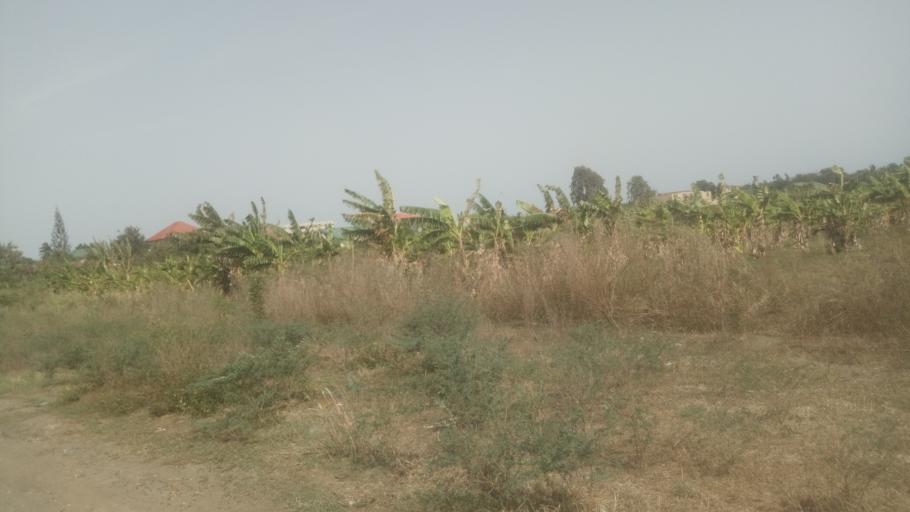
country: GH
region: Central
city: Winneba
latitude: 5.3777
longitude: -0.6496
